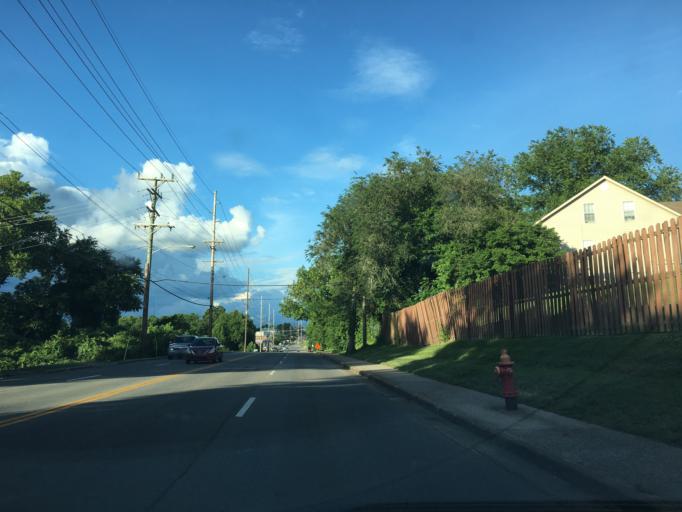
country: US
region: Tennessee
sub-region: Davidson County
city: Oak Hill
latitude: 36.0755
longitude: -86.7292
